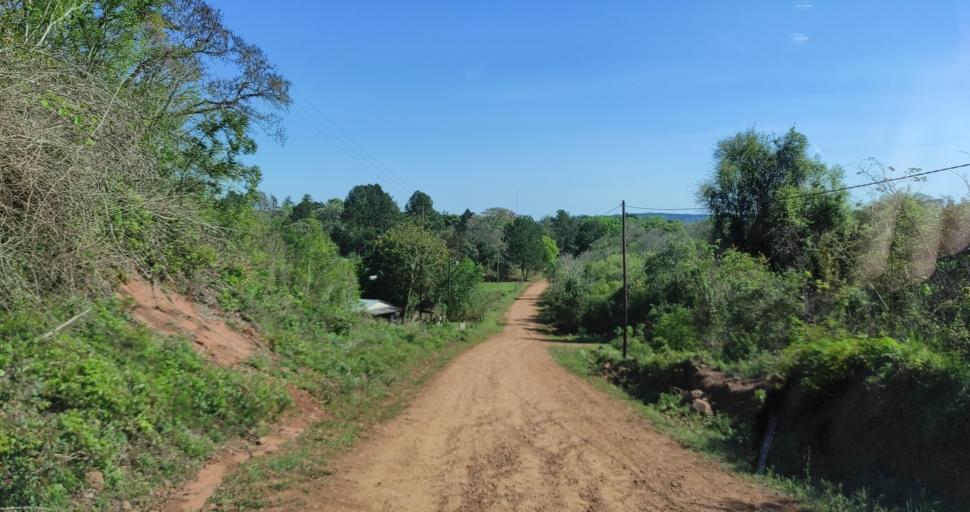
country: AR
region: Misiones
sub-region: Departamento de Candelaria
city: Loreto
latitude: -27.3141
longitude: -55.5361
